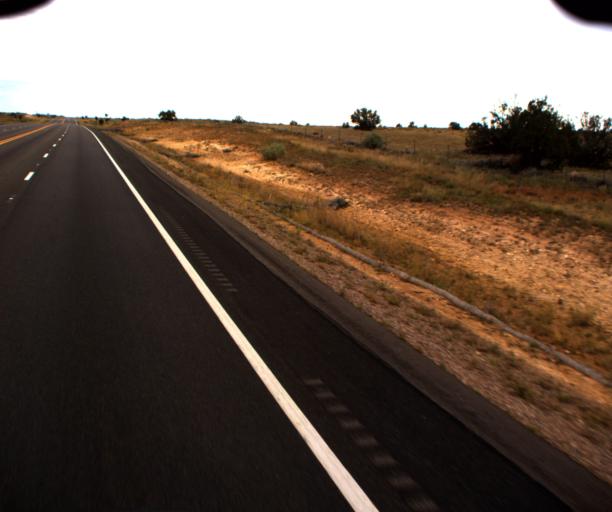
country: US
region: Arizona
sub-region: Navajo County
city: Snowflake
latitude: 34.5897
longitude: -110.0862
